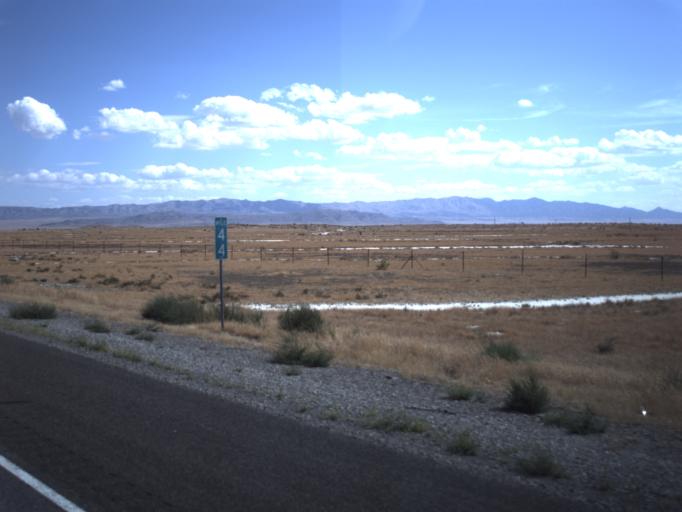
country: US
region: Utah
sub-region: Tooele County
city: Grantsville
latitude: 40.7258
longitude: -113.2070
